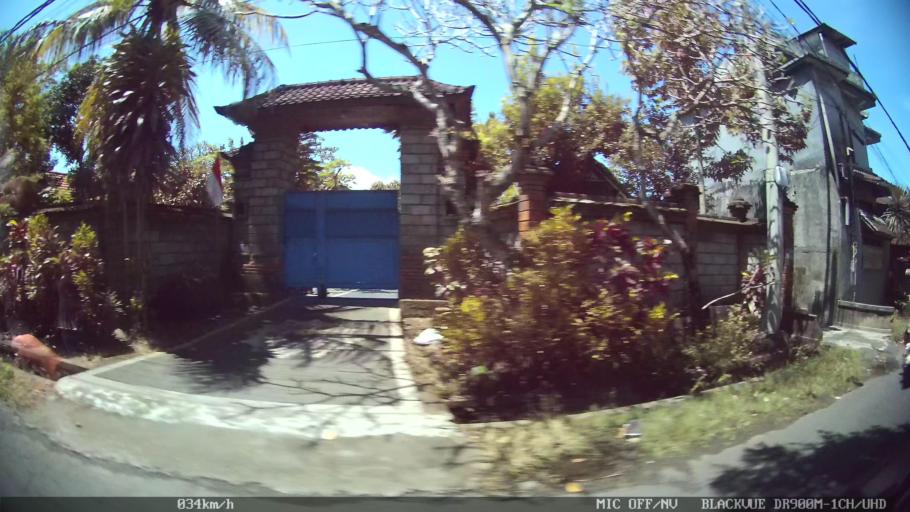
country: ID
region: Bali
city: Klungkung
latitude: -8.5609
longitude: 115.3385
